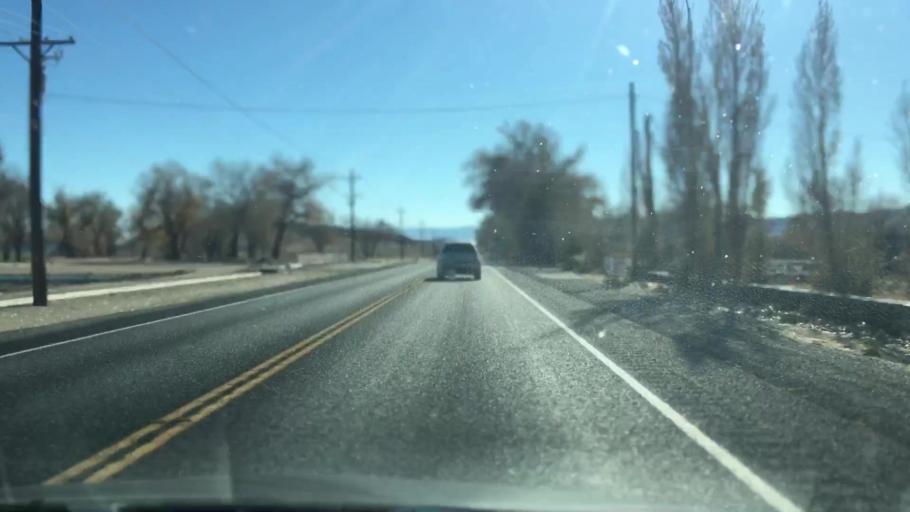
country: US
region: Nevada
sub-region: Lyon County
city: Yerington
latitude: 39.0330
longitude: -119.1816
